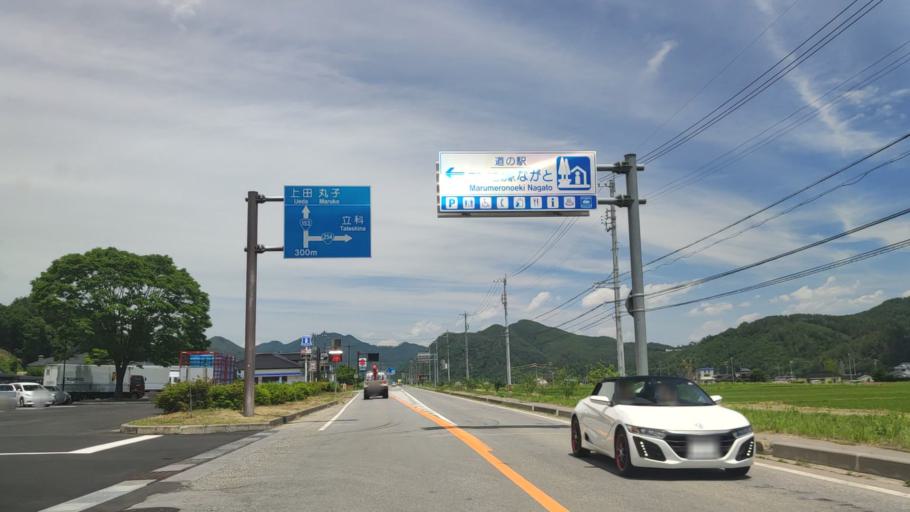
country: JP
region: Nagano
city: Kamimaruko
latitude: 36.2727
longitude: 138.2584
